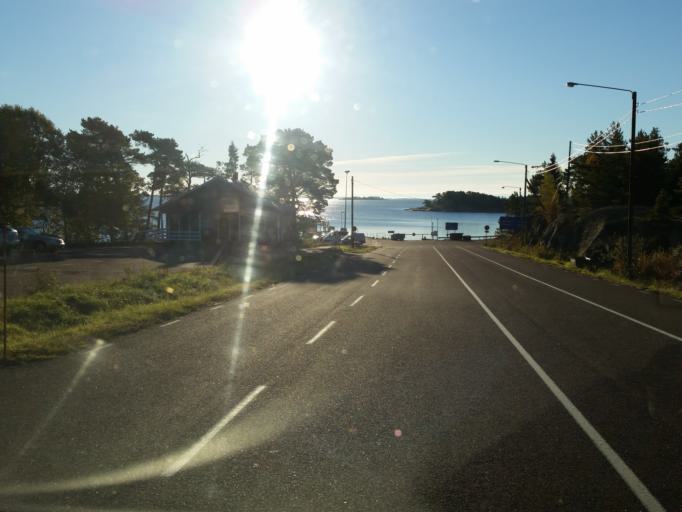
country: AX
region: Alands skaergard
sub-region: Vardoe
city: Vardoe
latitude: 60.2252
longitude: 20.4118
